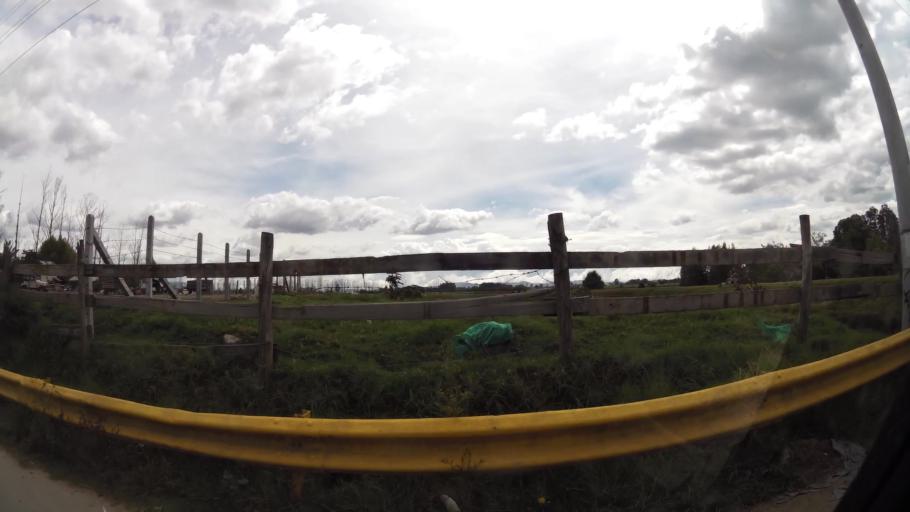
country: CO
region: Cundinamarca
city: Funza
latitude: 4.7259
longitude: -74.1489
